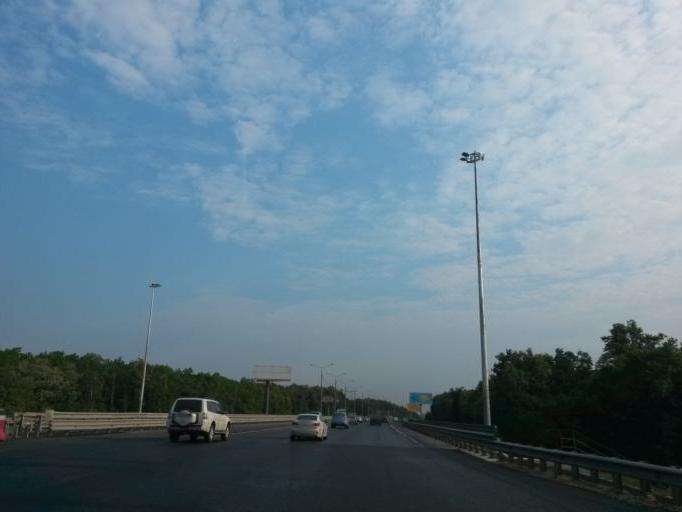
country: RU
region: Moscow
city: Annino
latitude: 55.5437
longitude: 37.6075
